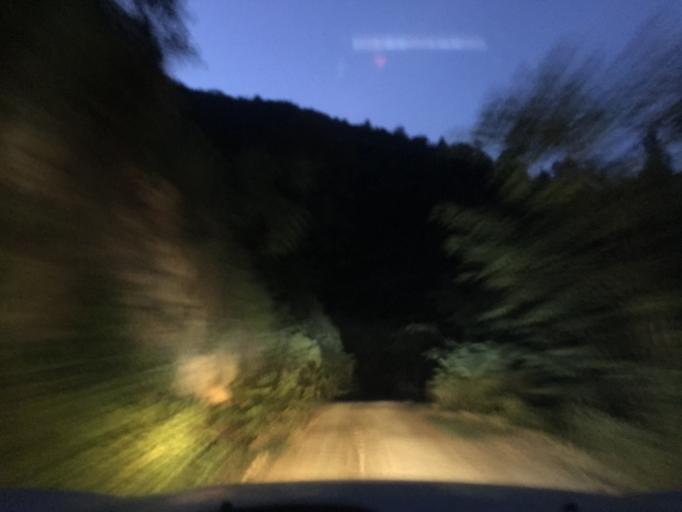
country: CN
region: Guangxi Zhuangzu Zizhiqu
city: Xinzhou
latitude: 25.3590
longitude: 105.7325
